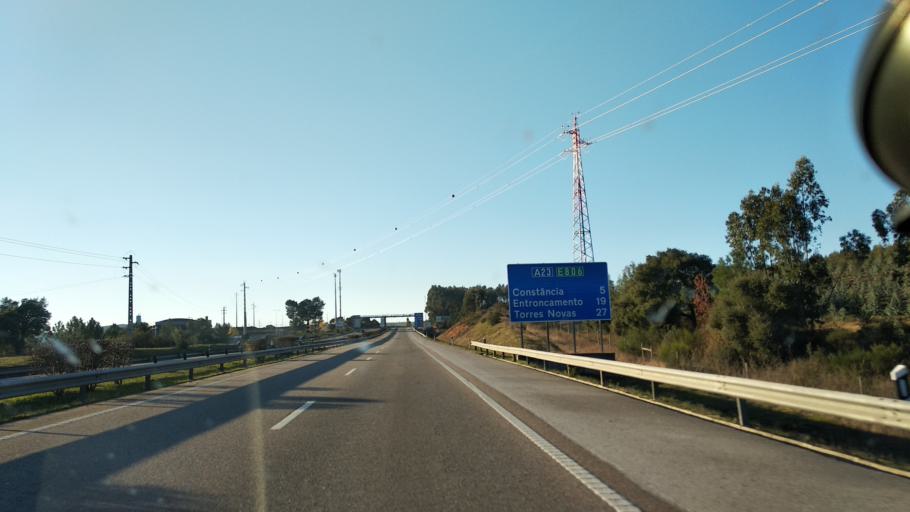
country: PT
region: Santarem
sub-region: Abrantes
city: Tramagal
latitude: 39.4871
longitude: -8.2833
